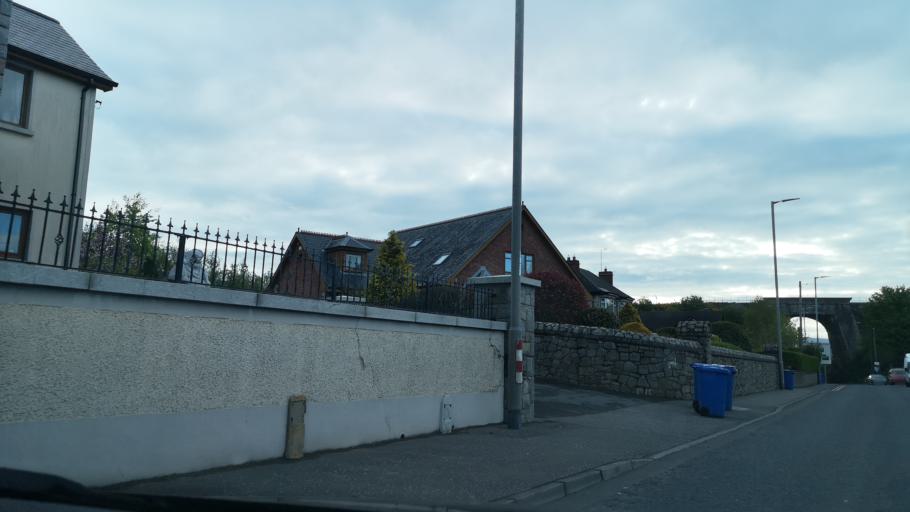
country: GB
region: Northern Ireland
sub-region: Newry and Mourne District
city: Newry
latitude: 54.1858
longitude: -6.3643
